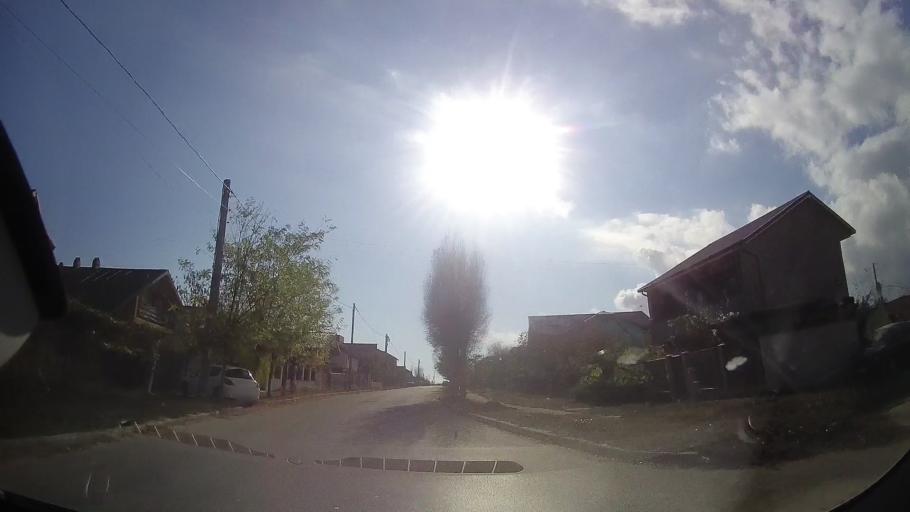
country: RO
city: Eforie Sud
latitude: 44.0167
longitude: 28.6473
